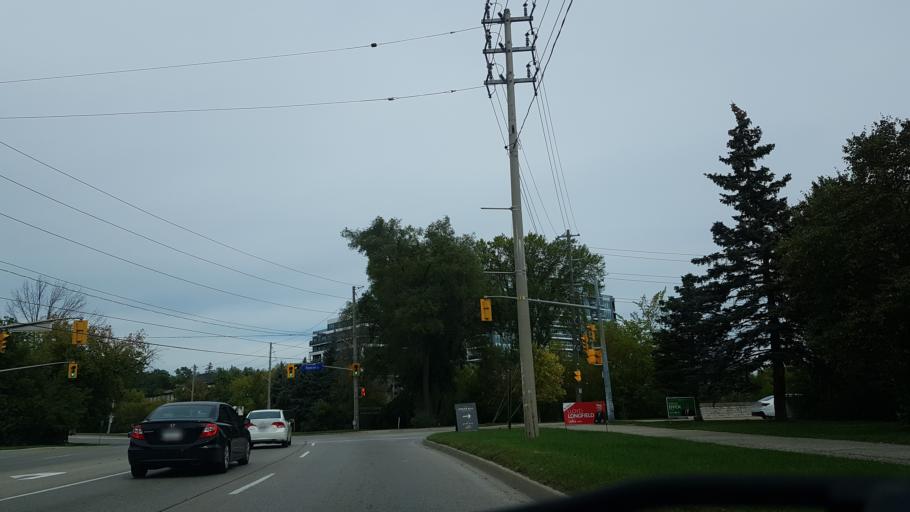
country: CA
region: Ontario
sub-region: Wellington County
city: Guelph
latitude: 43.5442
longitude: -80.2429
